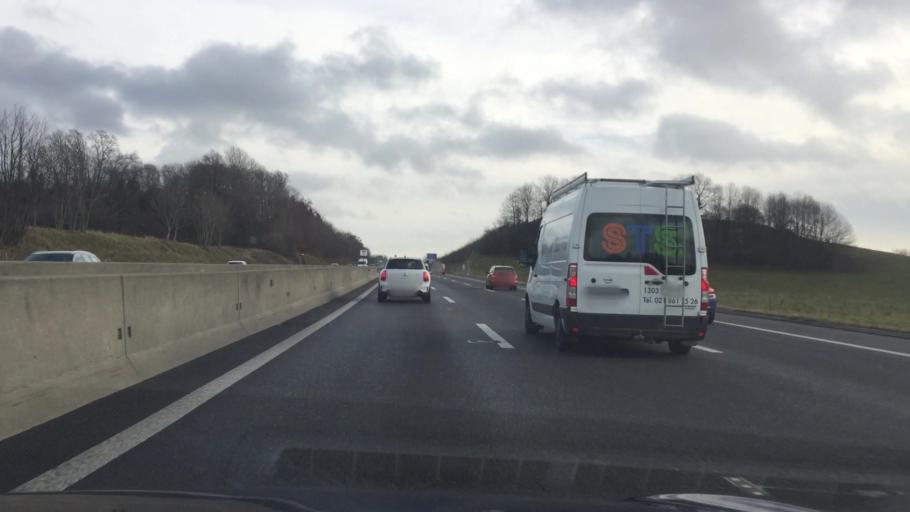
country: CH
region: Vaud
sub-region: Lausanne District
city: Romanel
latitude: 46.5538
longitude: 6.6039
